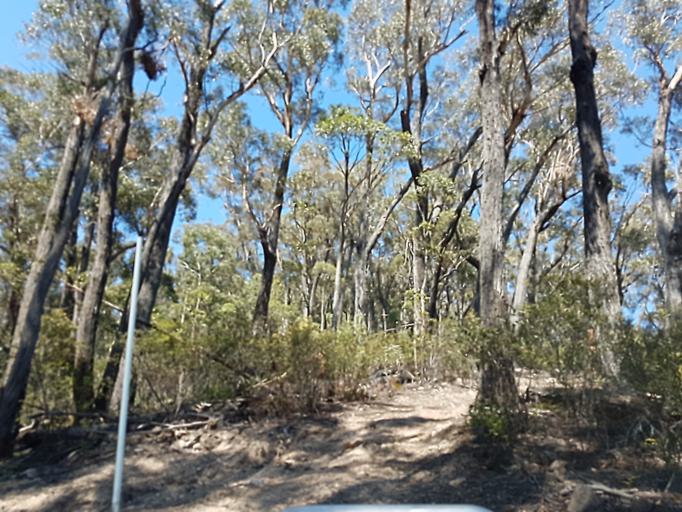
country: AU
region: Victoria
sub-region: East Gippsland
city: Lakes Entrance
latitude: -37.2878
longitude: 148.3281
